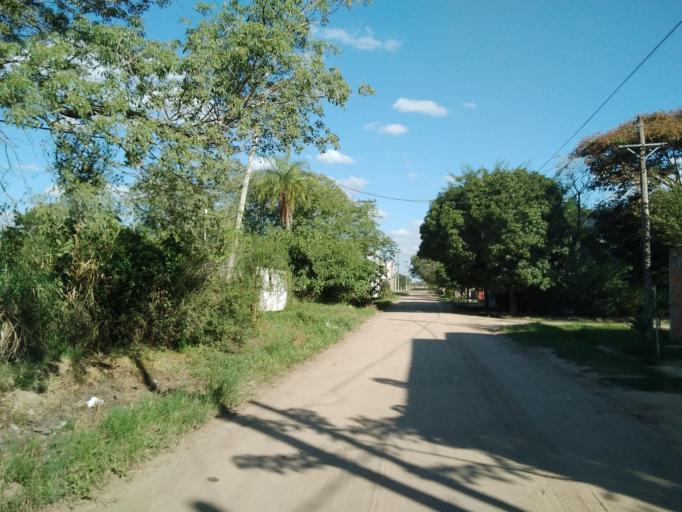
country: AR
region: Corrientes
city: Corrientes
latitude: -27.4608
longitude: -58.7739
